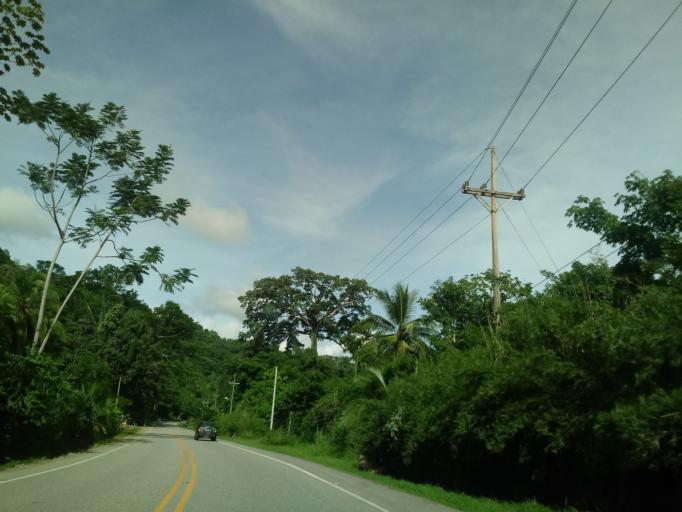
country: CR
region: San Jose
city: Daniel Flores
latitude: 9.2053
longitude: -83.7993
